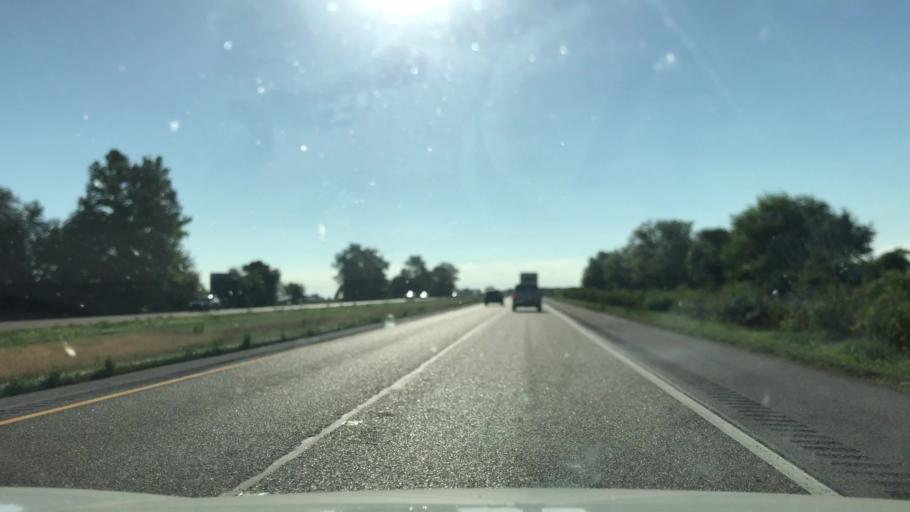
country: US
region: Illinois
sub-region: Saint Clair County
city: Lebanon
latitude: 38.5506
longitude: -89.7939
